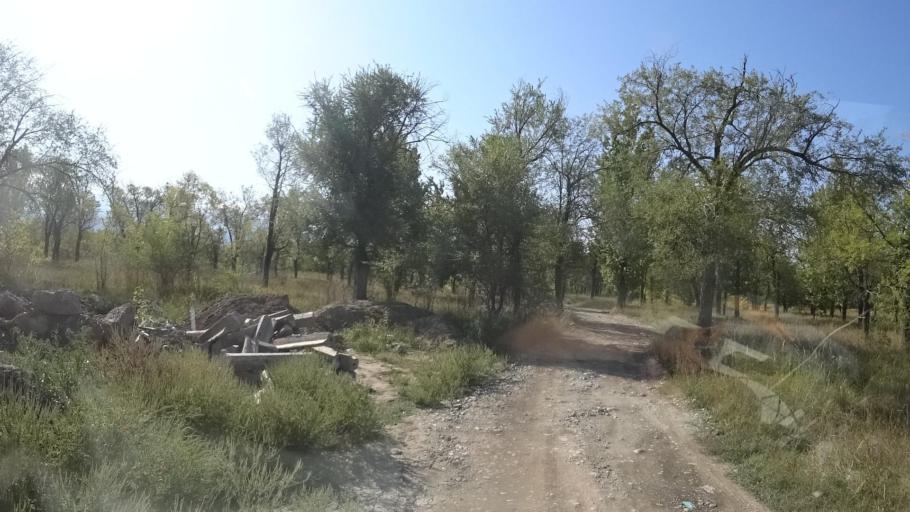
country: KZ
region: Almaty Oblysy
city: Pervomayskiy
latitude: 43.3330
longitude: 76.9994
